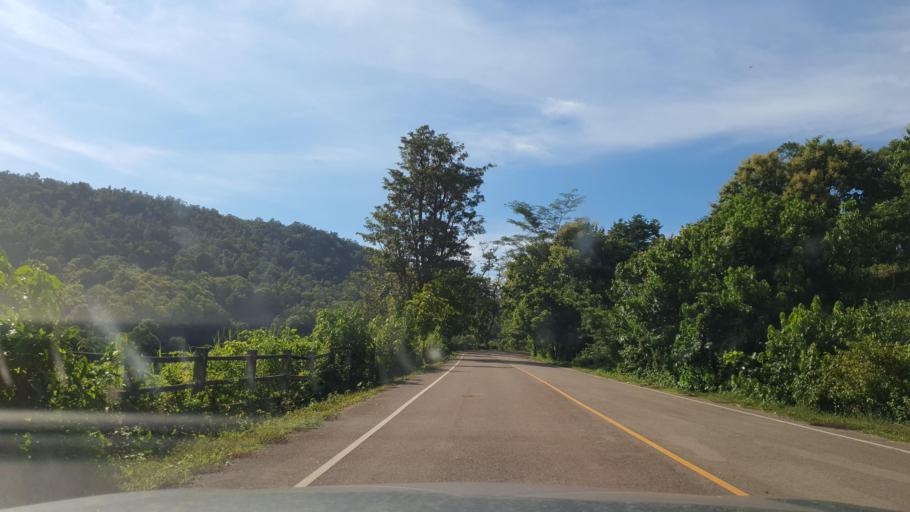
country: TH
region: Chiang Mai
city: Mae On
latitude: 18.7426
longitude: 99.3020
